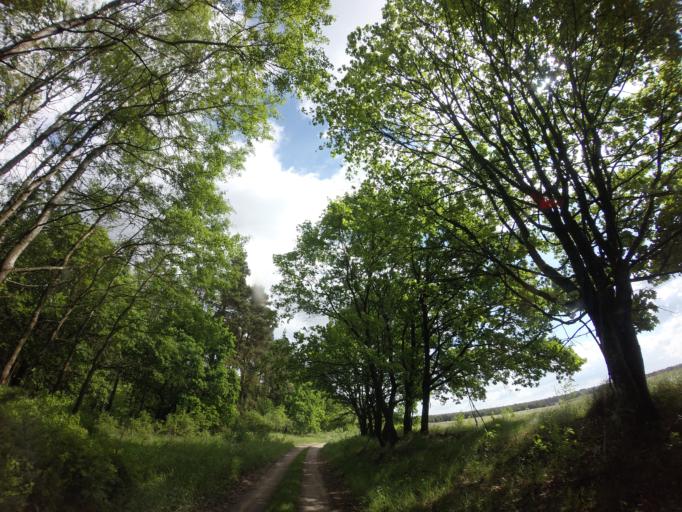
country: PL
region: West Pomeranian Voivodeship
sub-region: Powiat choszczenski
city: Drawno
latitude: 53.1767
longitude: 15.6834
